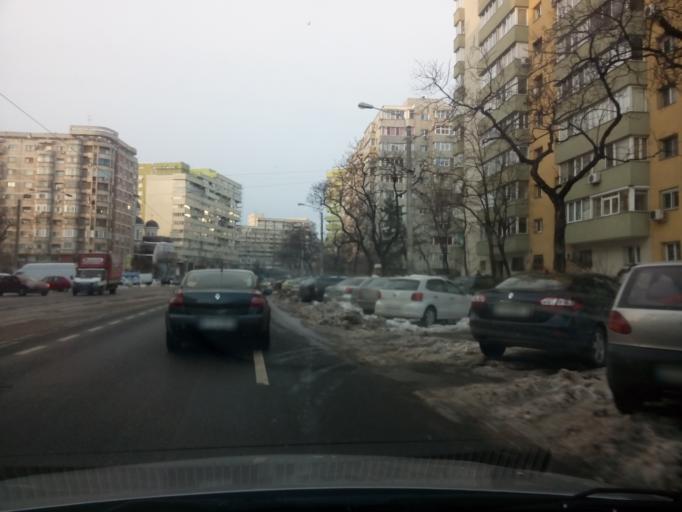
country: RO
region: Ilfov
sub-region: Comuna Fundeni-Dobroesti
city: Fundeni
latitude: 44.4402
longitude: 26.1579
